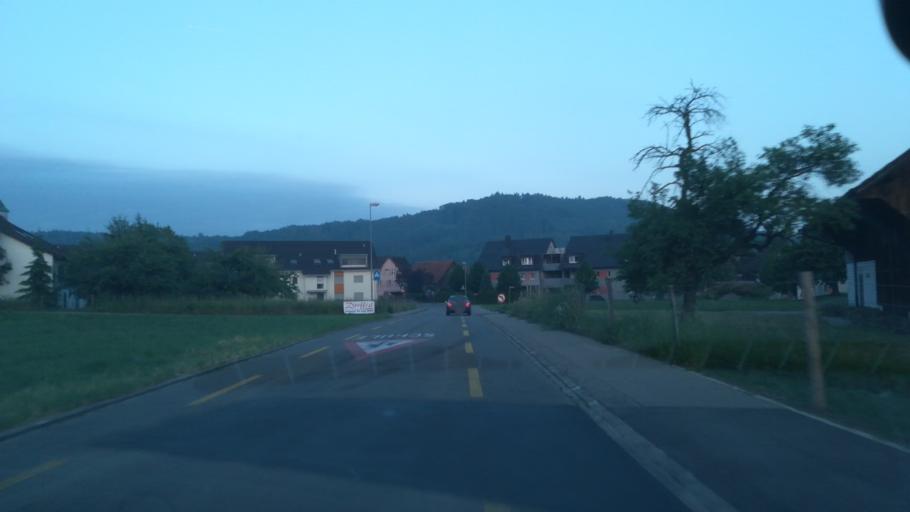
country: CH
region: Schaffhausen
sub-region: Bezirk Stein
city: Ramsen
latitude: 47.7082
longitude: 8.8141
